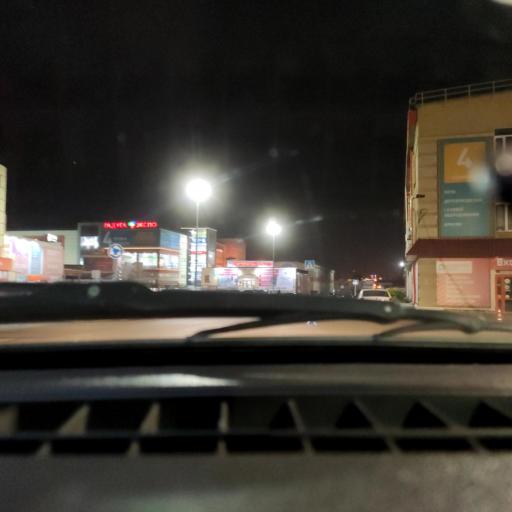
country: RU
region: Bashkortostan
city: Ufa
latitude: 54.8032
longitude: 56.0955
